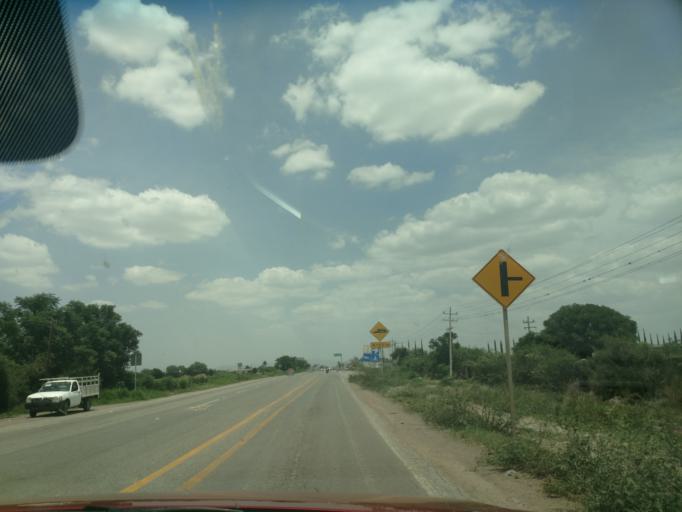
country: MX
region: San Luis Potosi
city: Ciudad Fernandez
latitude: 21.9427
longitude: -100.0441
